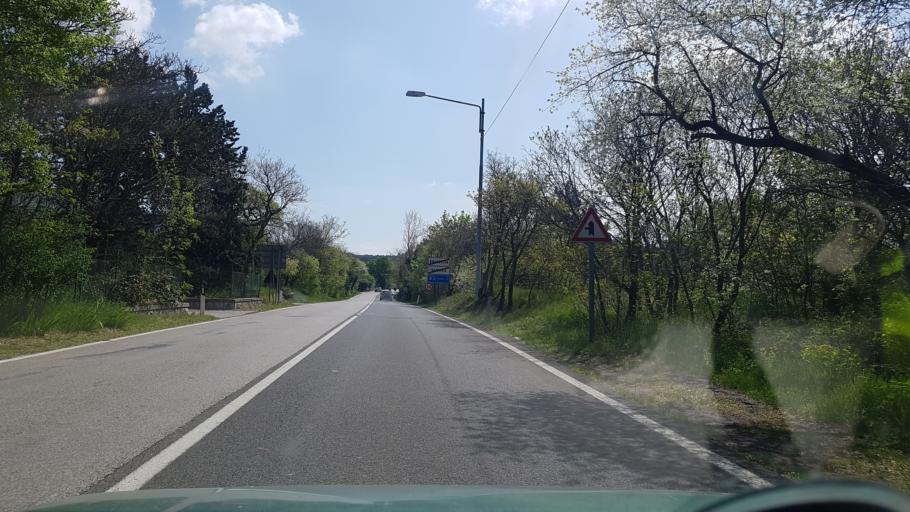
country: IT
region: Friuli Venezia Giulia
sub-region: Provincia di Trieste
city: Dolina
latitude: 45.6392
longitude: 13.8668
